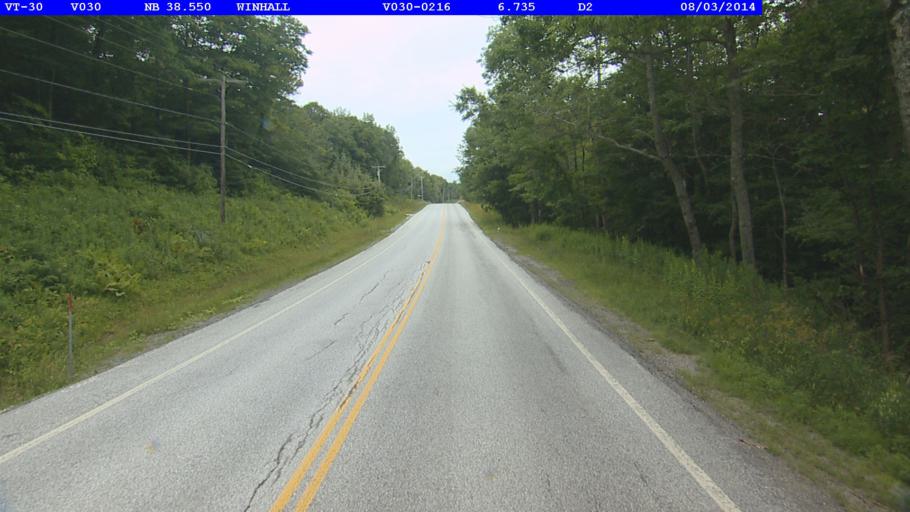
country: US
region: Vermont
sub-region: Bennington County
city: Manchester Center
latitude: 43.1946
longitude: -72.9554
